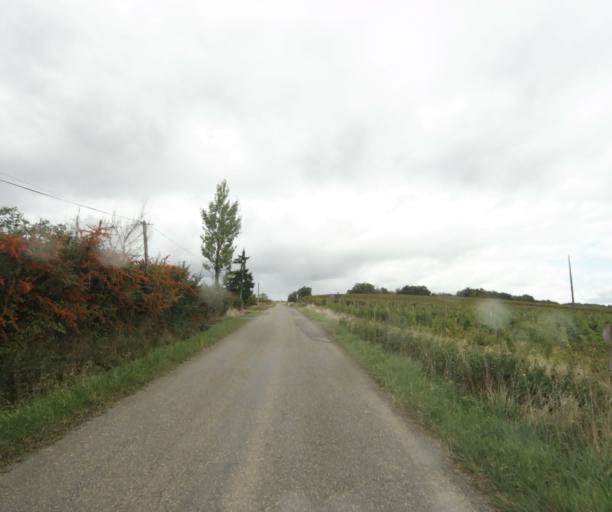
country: FR
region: Midi-Pyrenees
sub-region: Departement du Gers
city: Nogaro
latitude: 43.8250
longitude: -0.0396
